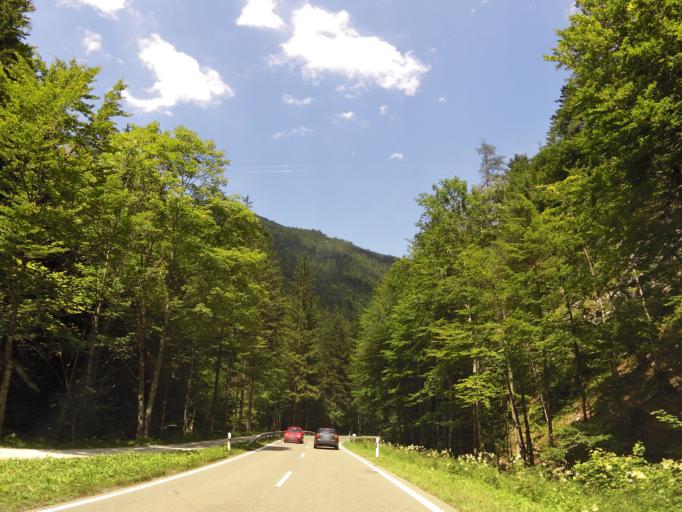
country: DE
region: Bavaria
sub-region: Upper Bavaria
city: Ruhpolding
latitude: 47.7127
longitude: 12.6268
